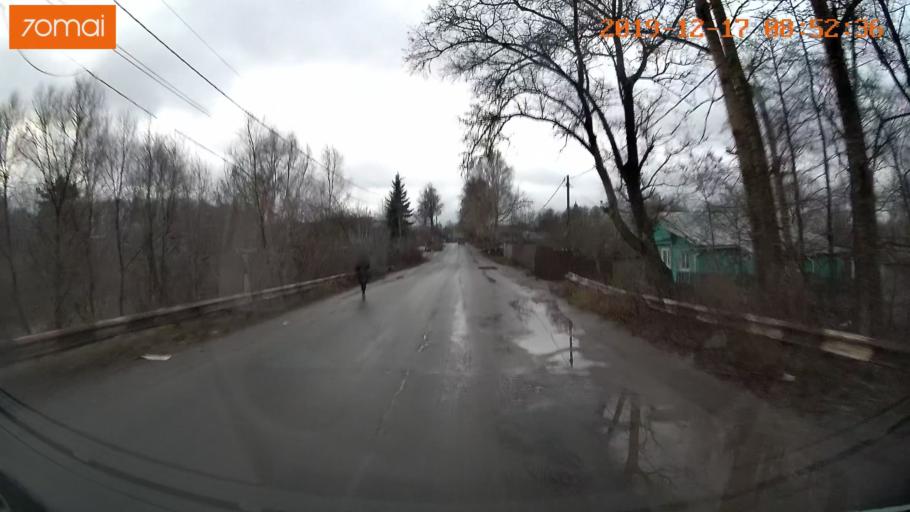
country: RU
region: Vladimir
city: Kosterevo
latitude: 55.9472
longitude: 39.6324
